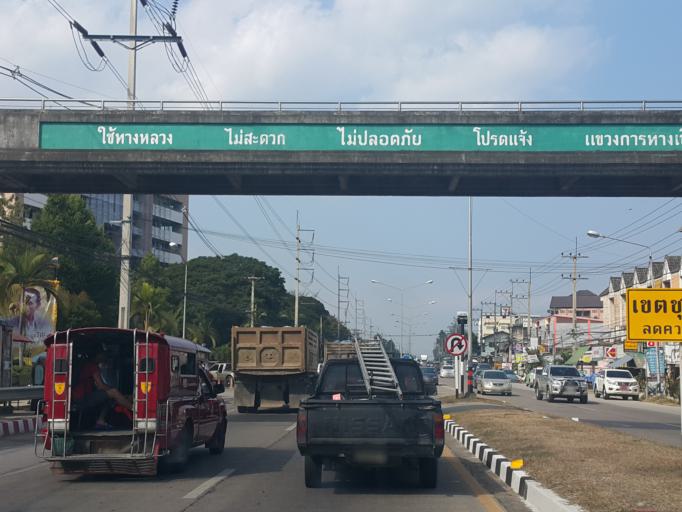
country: TH
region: Chiang Mai
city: Chiang Mai
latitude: 18.8511
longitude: 98.9693
